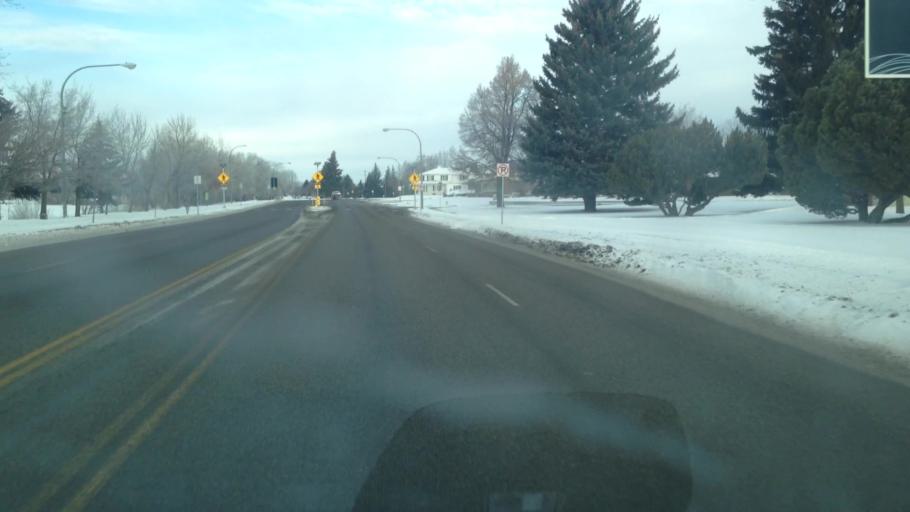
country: US
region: Idaho
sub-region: Bonneville County
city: Idaho Falls
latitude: 43.5030
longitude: -112.0444
